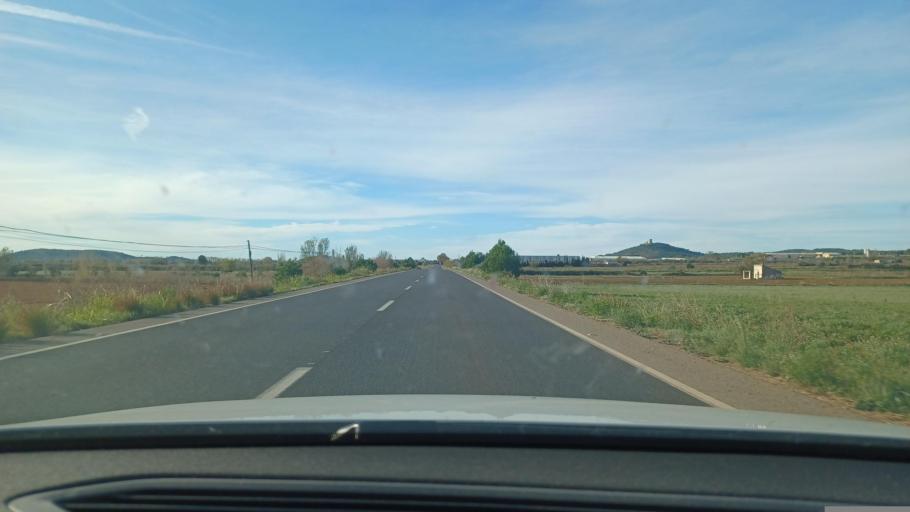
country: ES
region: Catalonia
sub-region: Provincia de Tarragona
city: Ulldecona
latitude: 40.6132
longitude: 0.4648
